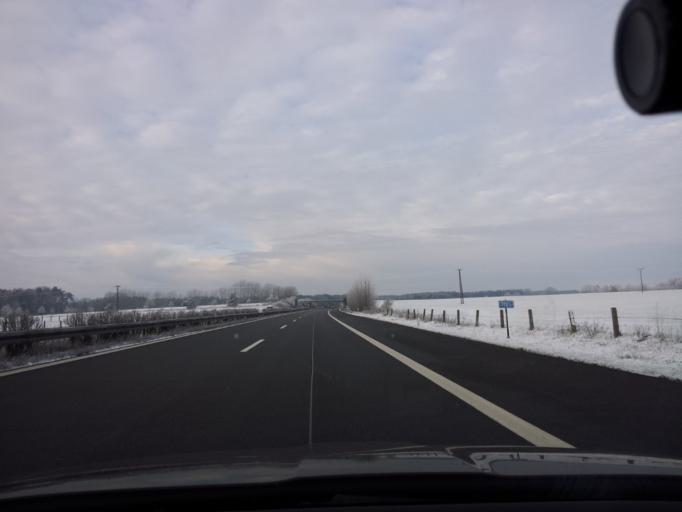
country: DE
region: Mecklenburg-Vorpommern
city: Spornitz
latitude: 53.3691
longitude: 11.6640
